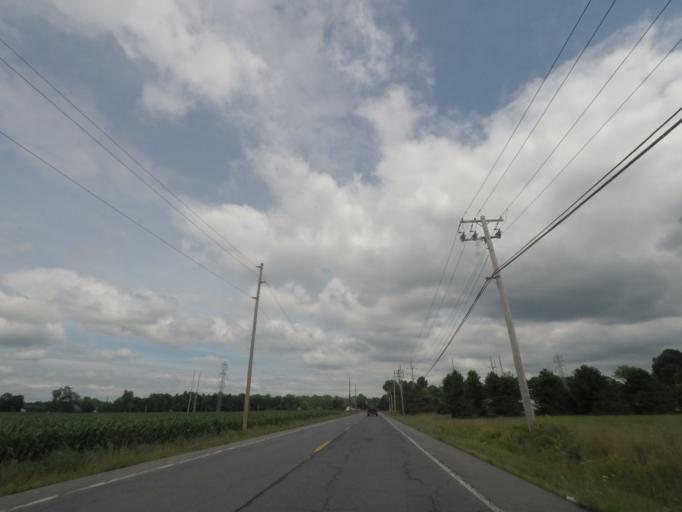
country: US
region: New York
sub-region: Saratoga County
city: Stillwater
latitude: 42.9084
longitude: -73.6117
